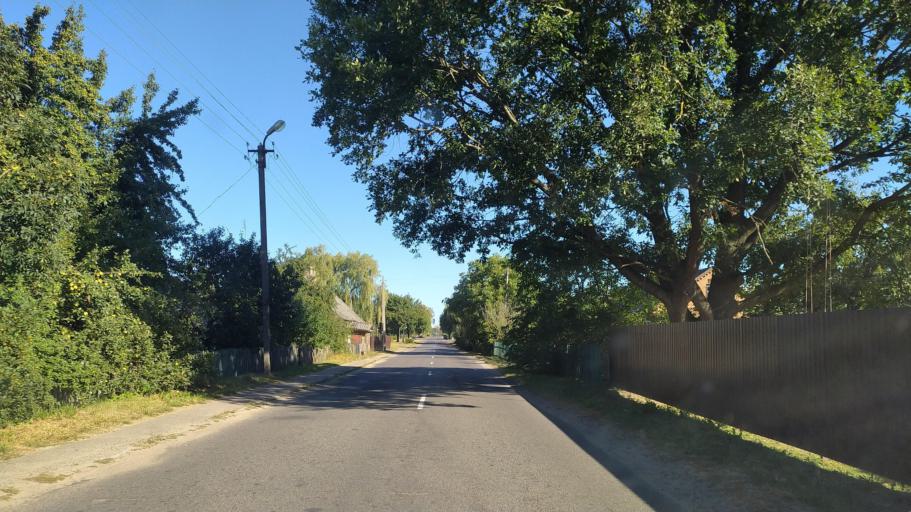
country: BY
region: Brest
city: Pruzhany
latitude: 52.4855
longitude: 24.7075
